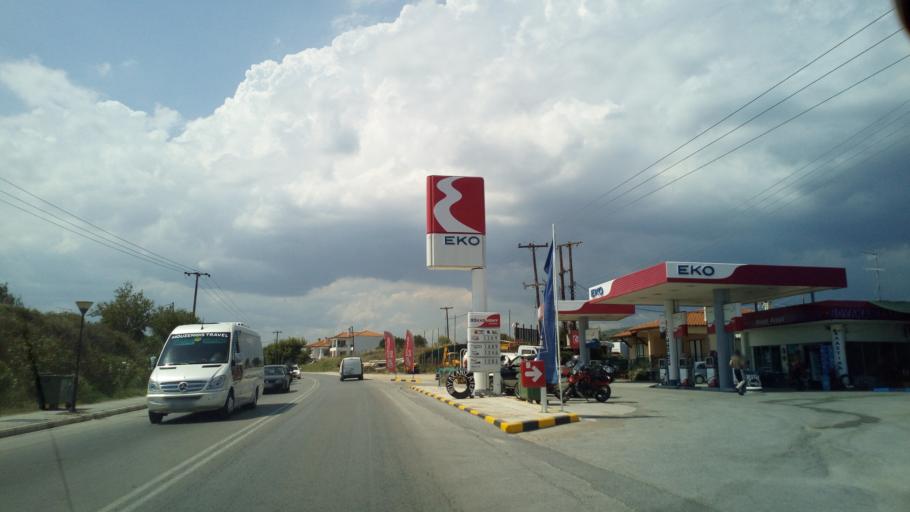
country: GR
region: Central Macedonia
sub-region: Nomos Chalkidikis
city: Nikiti
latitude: 40.2253
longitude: 23.6648
